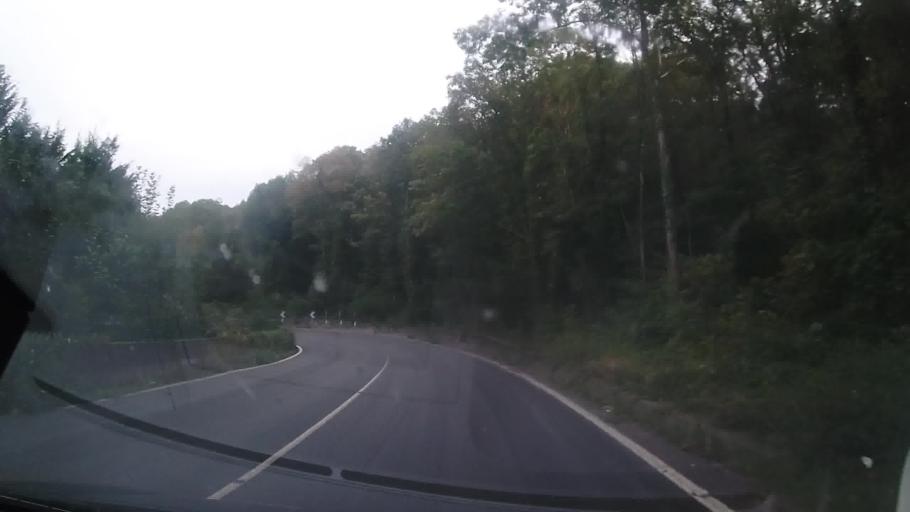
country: FR
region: Ile-de-France
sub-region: Departement de l'Essonne
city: Dourdan
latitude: 48.5620
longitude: 1.9863
